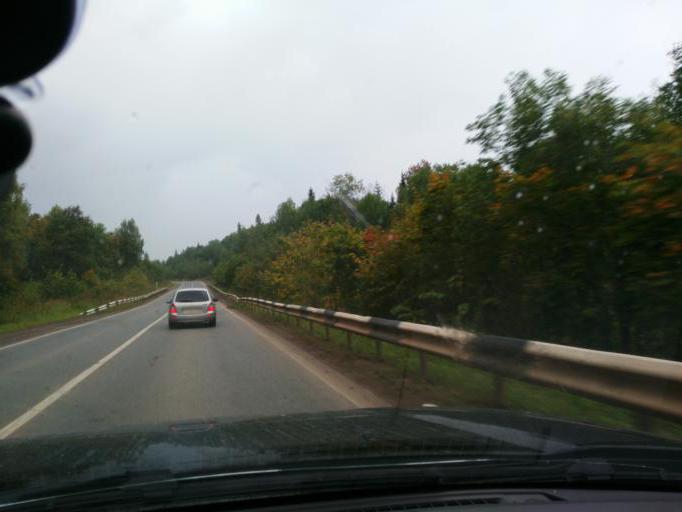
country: RU
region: Perm
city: Barda
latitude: 56.8918
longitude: 55.7785
